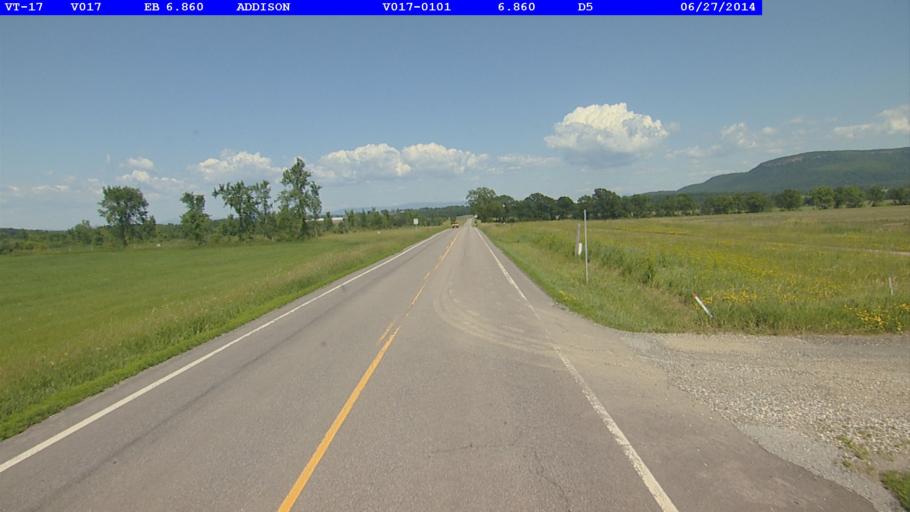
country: US
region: Vermont
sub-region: Addison County
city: Vergennes
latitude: 44.0861
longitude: -73.3327
